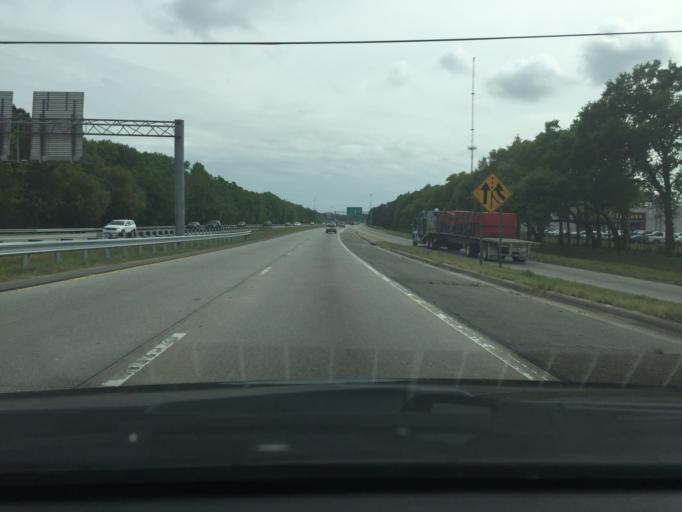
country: US
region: Georgia
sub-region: Chatham County
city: Savannah
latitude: 32.0522
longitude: -81.1424
